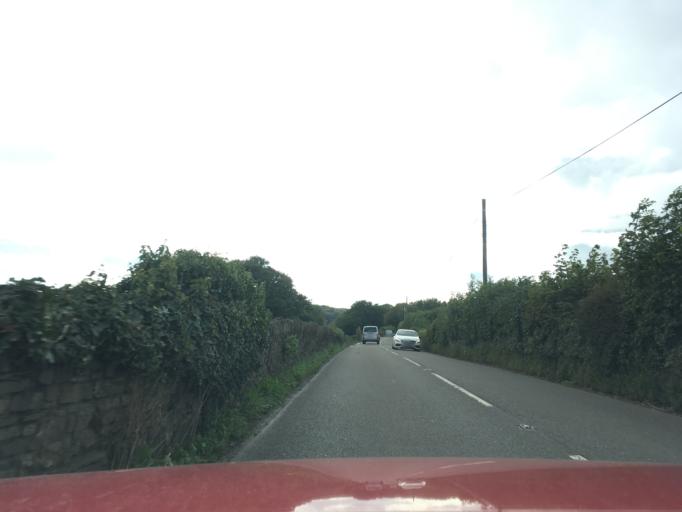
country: GB
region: England
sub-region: Devon
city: Modbury
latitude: 50.3496
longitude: -3.9161
